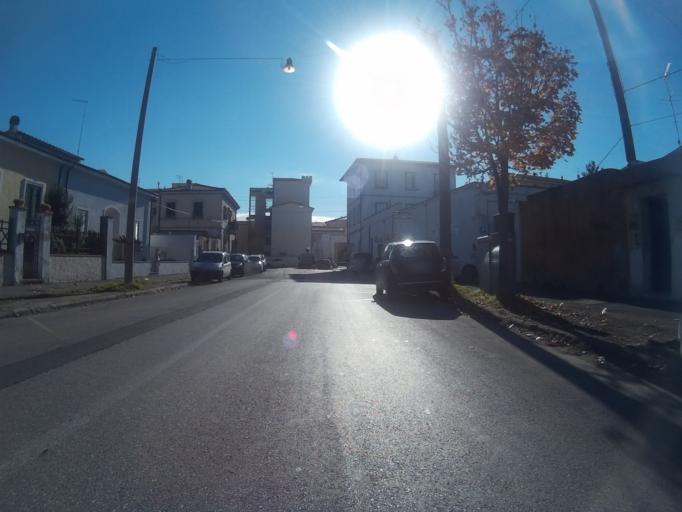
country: IT
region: Tuscany
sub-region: Provincia di Livorno
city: Livorno
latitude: 43.5619
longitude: 10.3188
